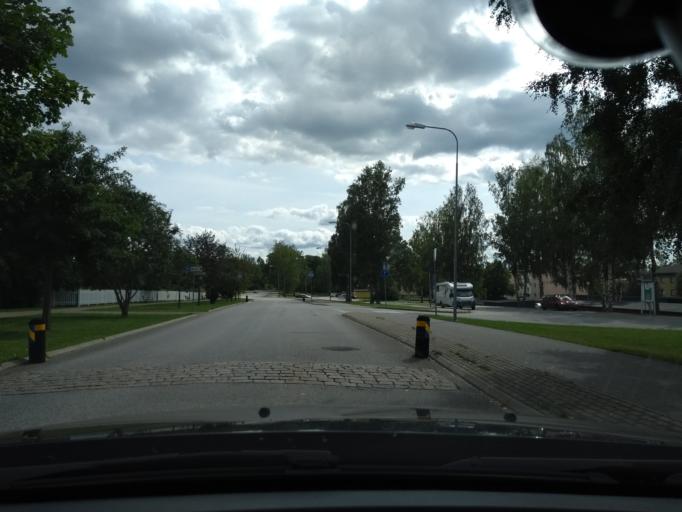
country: SE
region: Kalmar
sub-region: Vimmerby Kommun
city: Vimmerby
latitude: 57.6754
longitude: 15.8550
